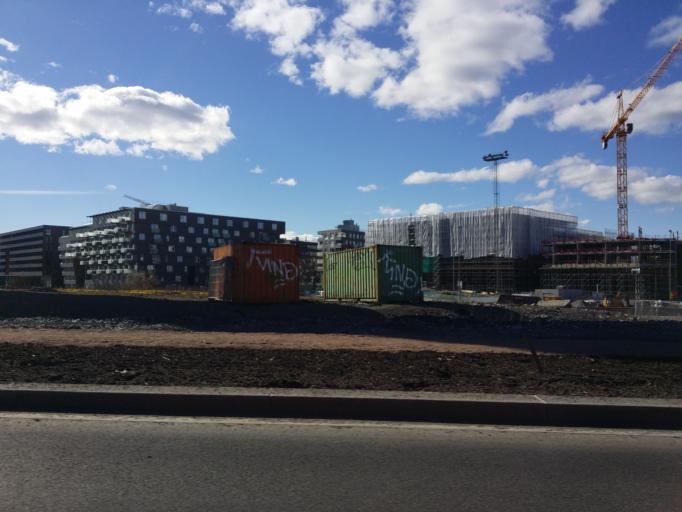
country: NO
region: Oslo
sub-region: Oslo
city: Oslo
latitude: 59.9030
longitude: 10.7593
